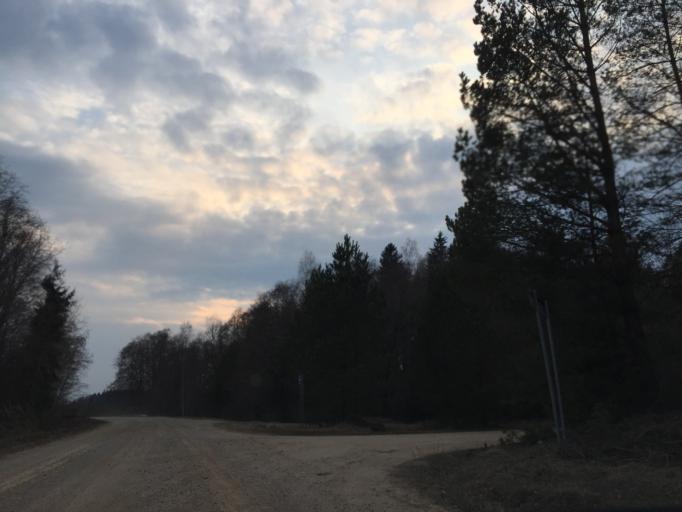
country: LV
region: Vecpiebalga
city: Vecpiebalga
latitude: 57.1327
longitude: 25.6455
